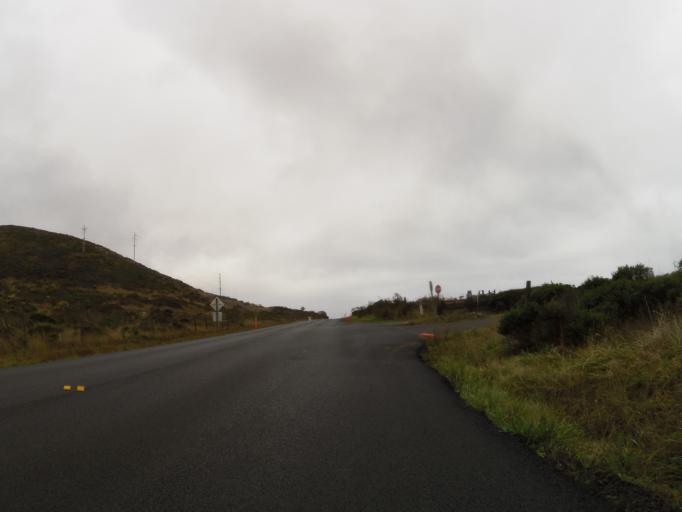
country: US
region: California
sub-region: Sonoma County
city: Monte Rio
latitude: 38.4311
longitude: -123.1088
